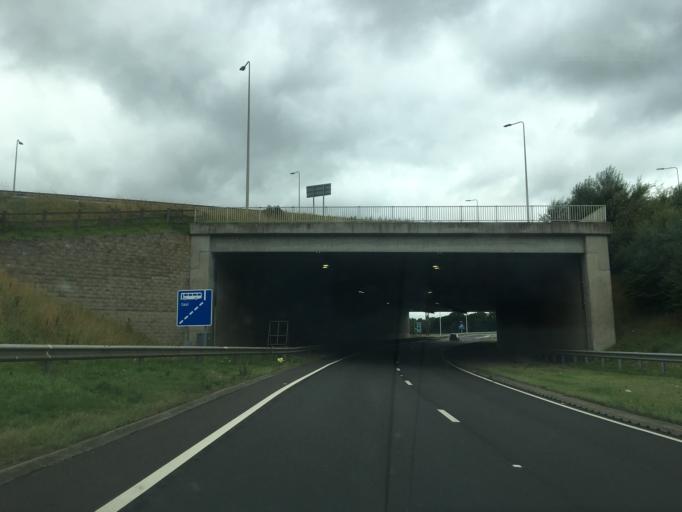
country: GB
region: Scotland
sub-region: Edinburgh
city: Queensferry
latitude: 55.9784
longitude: -3.3811
